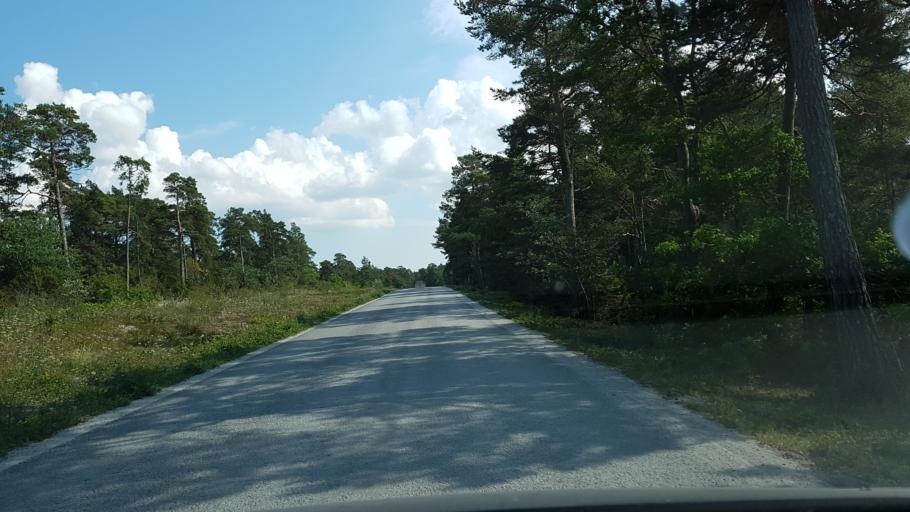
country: SE
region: Gotland
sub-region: Gotland
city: Visby
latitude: 57.8171
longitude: 18.5209
